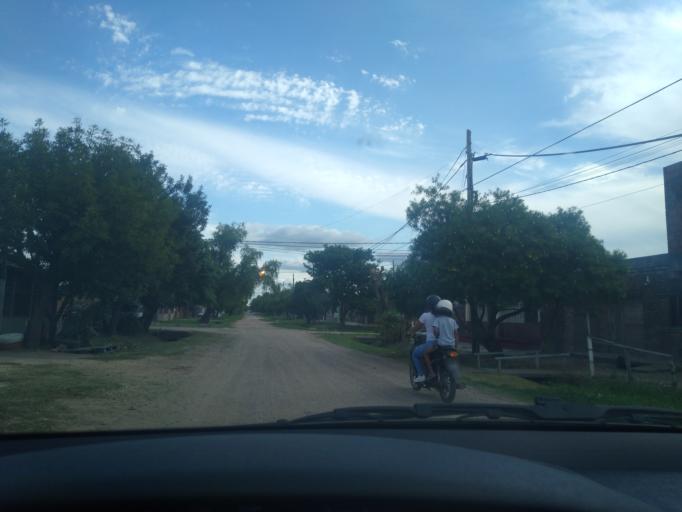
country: AR
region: Chaco
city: Resistencia
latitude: -27.4794
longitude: -58.9735
